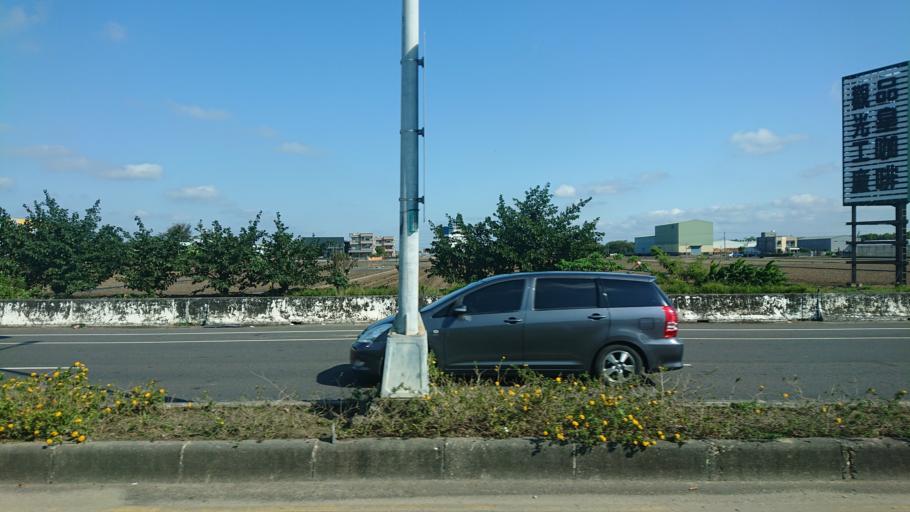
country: TW
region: Taiwan
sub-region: Chiayi
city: Taibao
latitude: 23.4457
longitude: 120.3638
